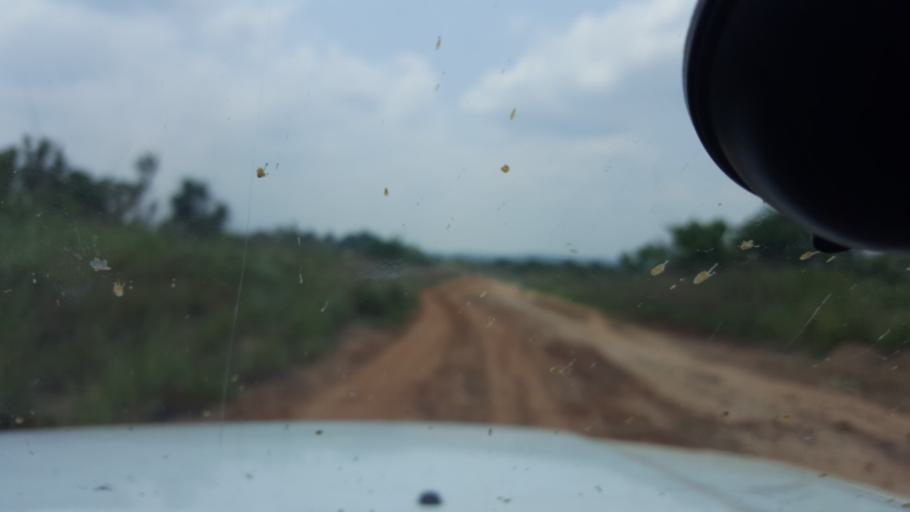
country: CD
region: Bandundu
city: Mushie
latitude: -3.7513
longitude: 16.6438
